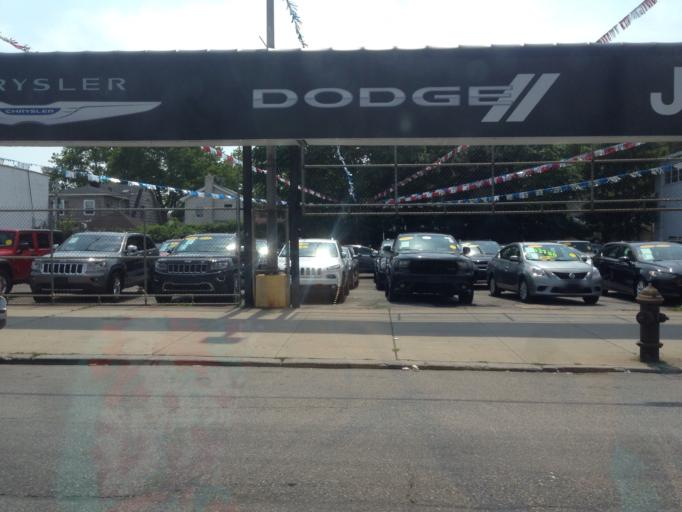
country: US
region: New York
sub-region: Kings County
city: Brooklyn
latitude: 40.6138
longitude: -73.9272
